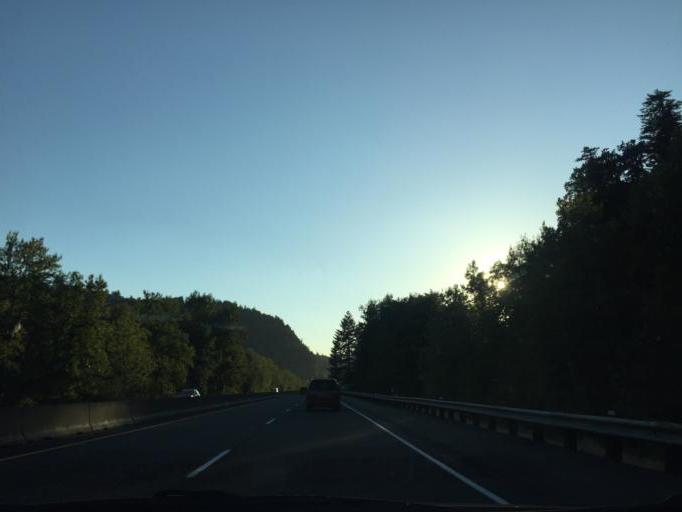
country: US
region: Washington
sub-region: Clark County
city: Washougal
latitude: 45.5428
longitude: -122.2475
